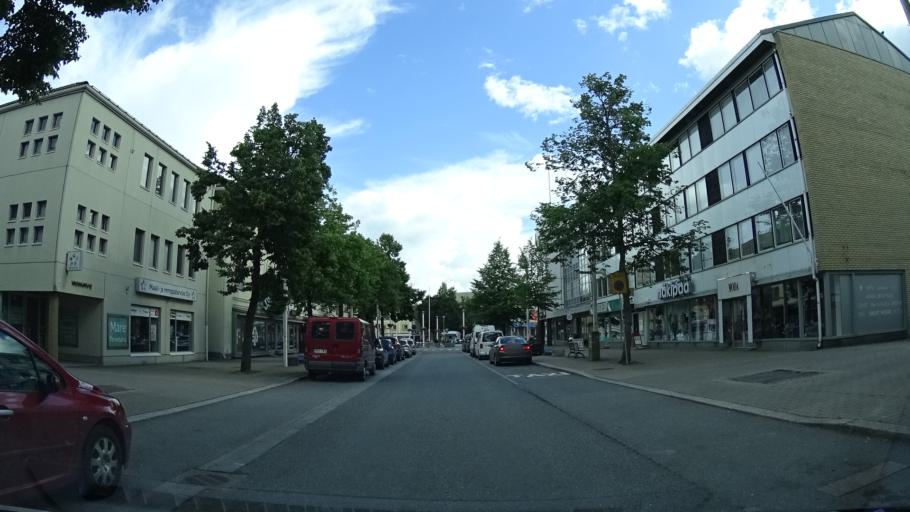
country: FI
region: Pirkanmaa
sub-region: Etelae-Pirkanmaa
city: Valkeakoski
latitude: 61.2674
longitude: 24.0284
